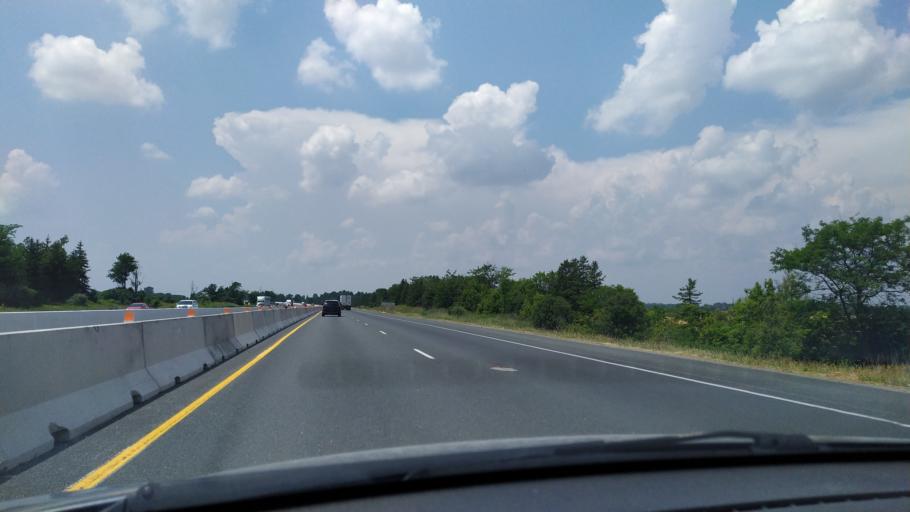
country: CA
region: Ontario
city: Dorchester
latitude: 42.9553
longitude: -81.0807
